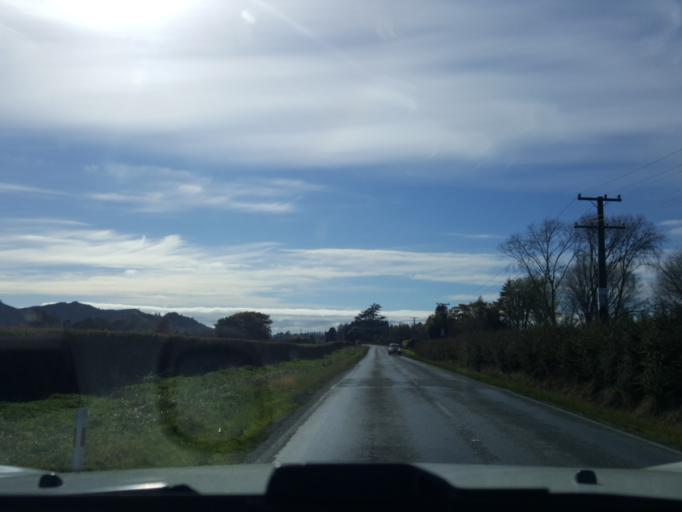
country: NZ
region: Waikato
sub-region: Waikato District
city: Ngaruawahia
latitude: -37.6036
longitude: 175.2000
